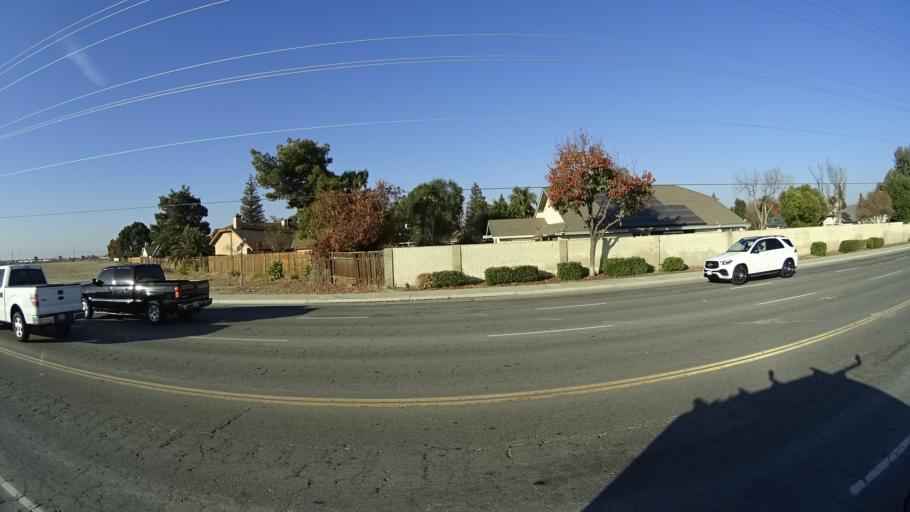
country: US
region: California
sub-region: Kern County
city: Greenfield
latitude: 35.2961
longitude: -119.0878
